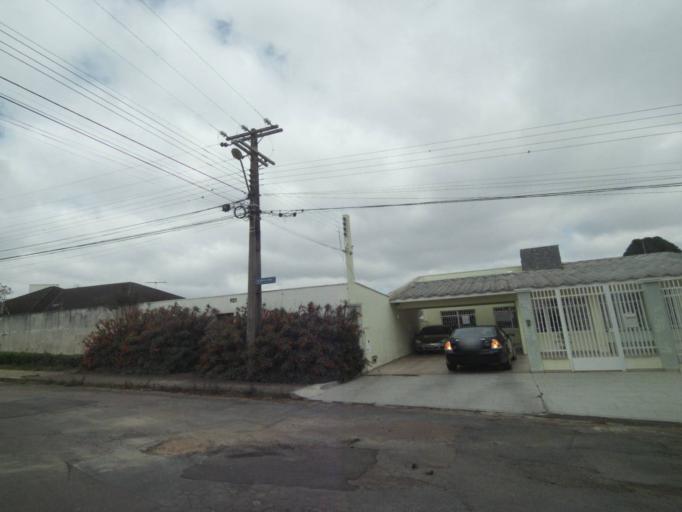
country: BR
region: Parana
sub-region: Curitiba
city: Curitiba
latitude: -25.4510
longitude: -49.3119
